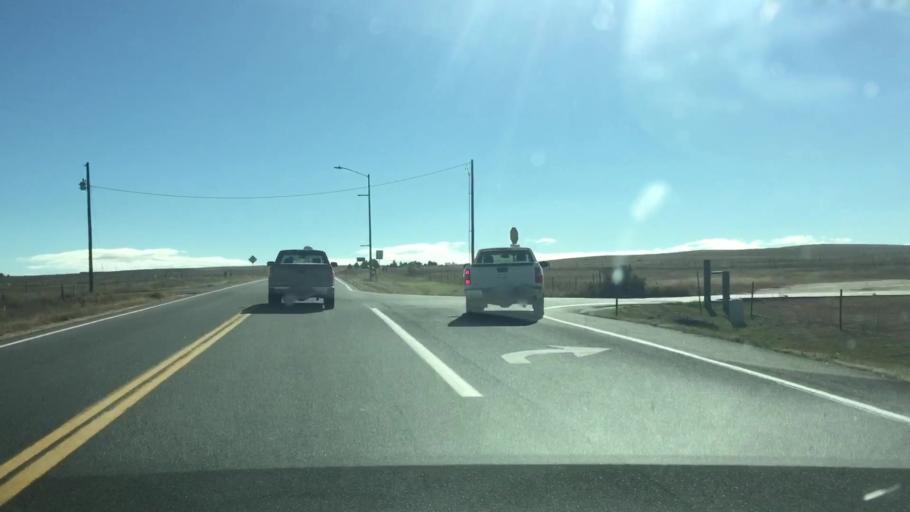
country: US
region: Colorado
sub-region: Elbert County
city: Kiowa
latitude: 39.3455
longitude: -104.4563
